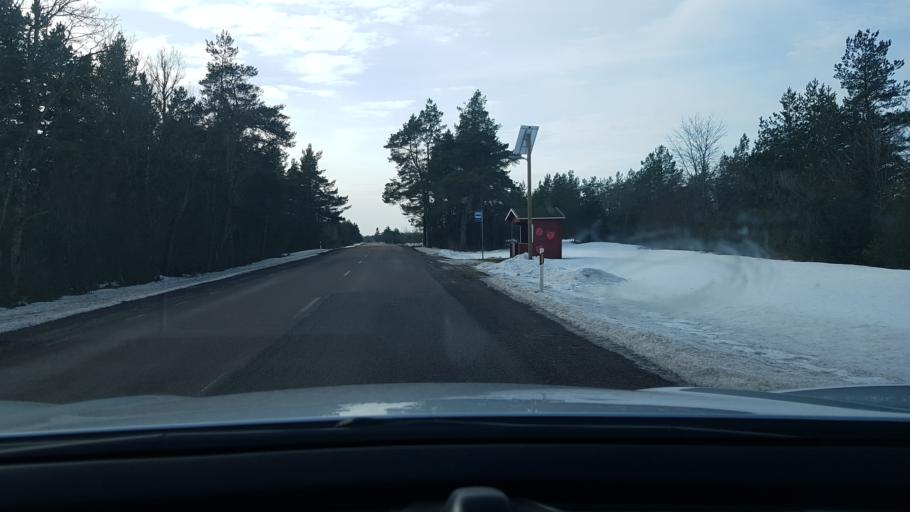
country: EE
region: Saare
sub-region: Kuressaare linn
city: Kuressaare
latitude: 58.3384
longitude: 22.5722
